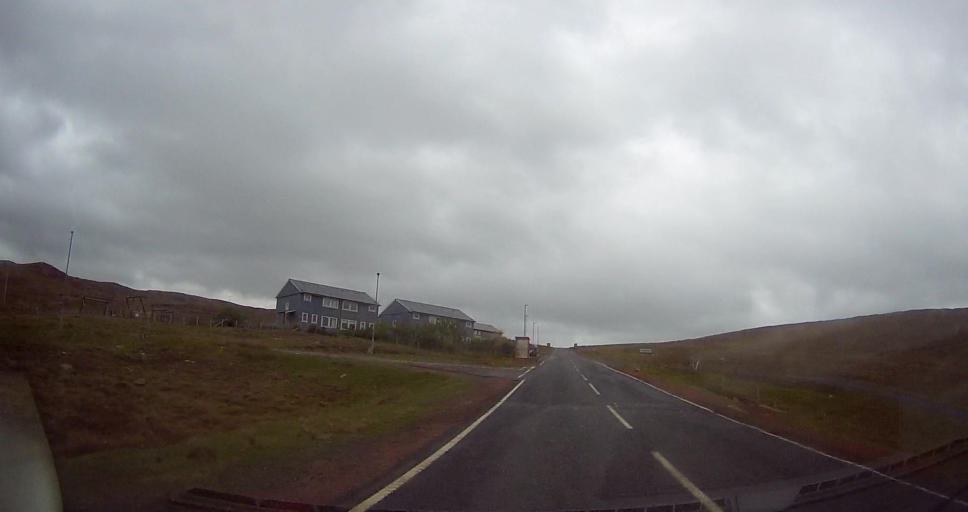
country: GB
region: Scotland
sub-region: Shetland Islands
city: Lerwick
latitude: 60.4884
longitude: -1.4508
